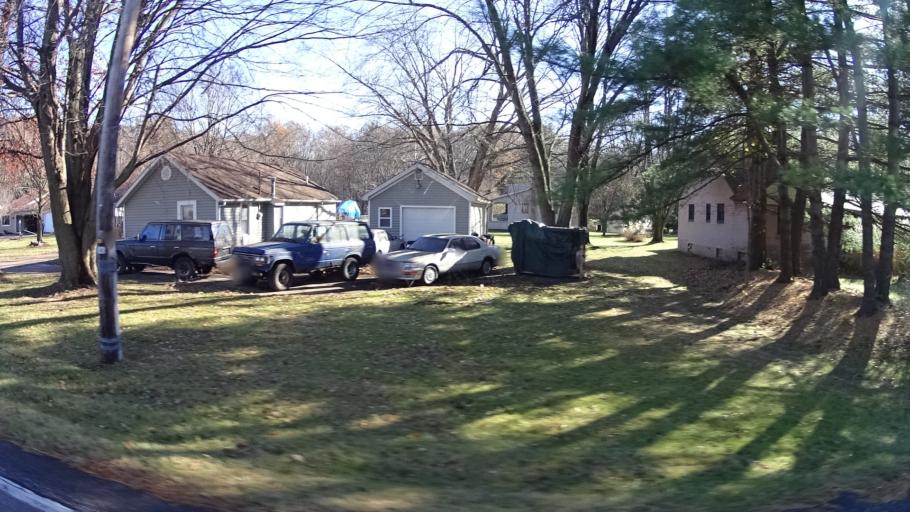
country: US
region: Ohio
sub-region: Cuyahoga County
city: North Olmsted
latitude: 41.4130
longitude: -81.9737
